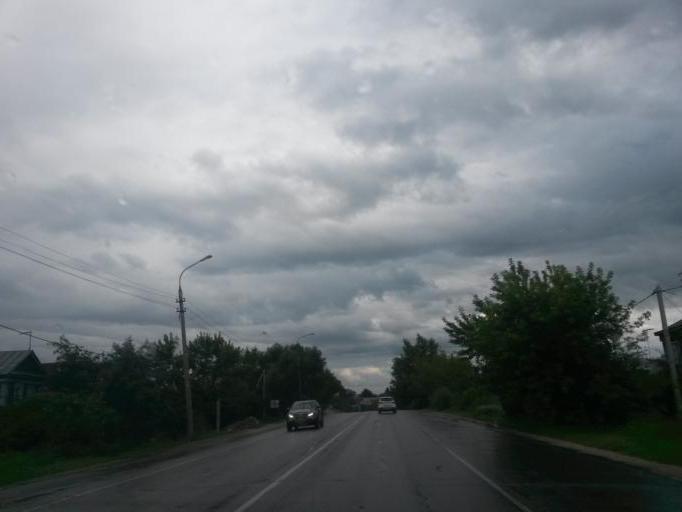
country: RU
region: Moskovskaya
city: Stolbovaya
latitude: 55.2780
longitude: 37.5100
